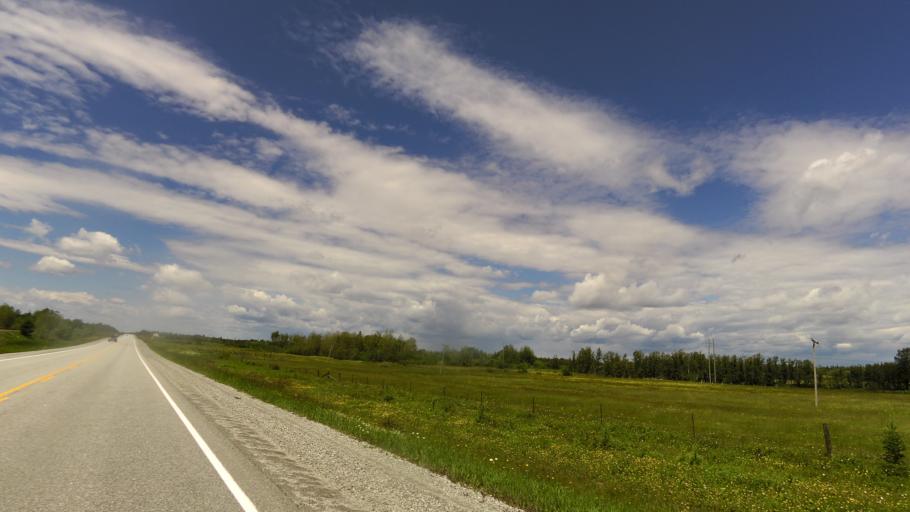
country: CA
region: Ontario
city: Kapuskasing
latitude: 49.2948
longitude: -81.9606
